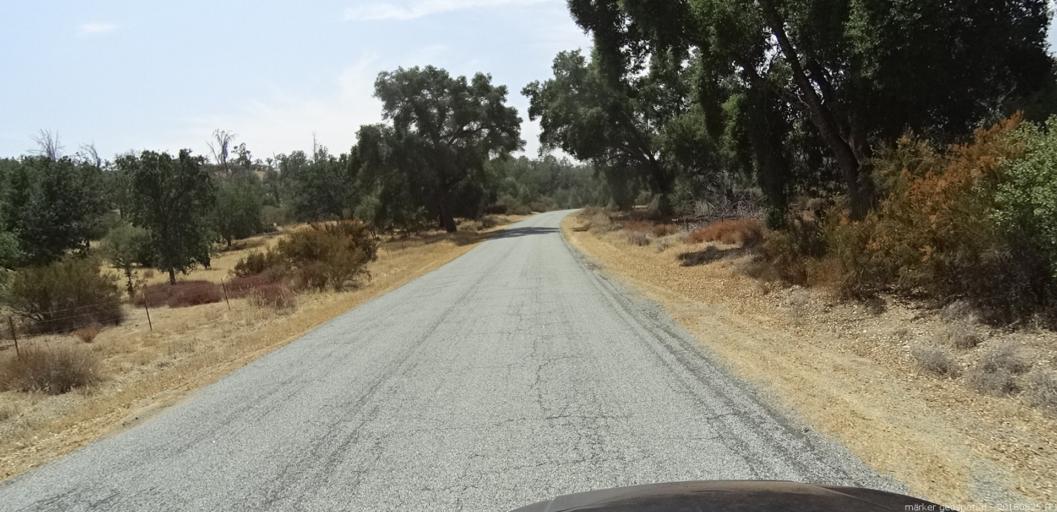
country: US
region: California
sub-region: San Luis Obispo County
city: San Miguel
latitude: 35.8949
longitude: -120.5548
